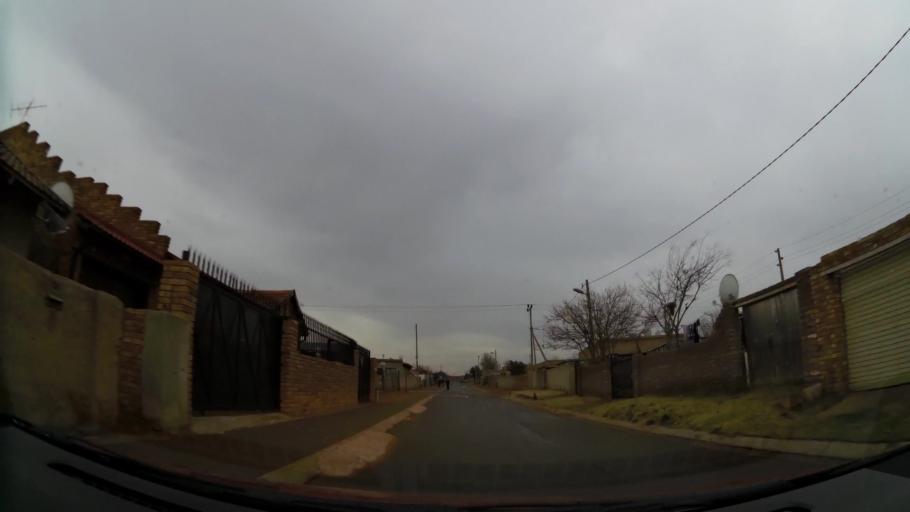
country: ZA
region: Gauteng
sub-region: City of Johannesburg Metropolitan Municipality
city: Roodepoort
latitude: -26.1762
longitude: 27.7877
